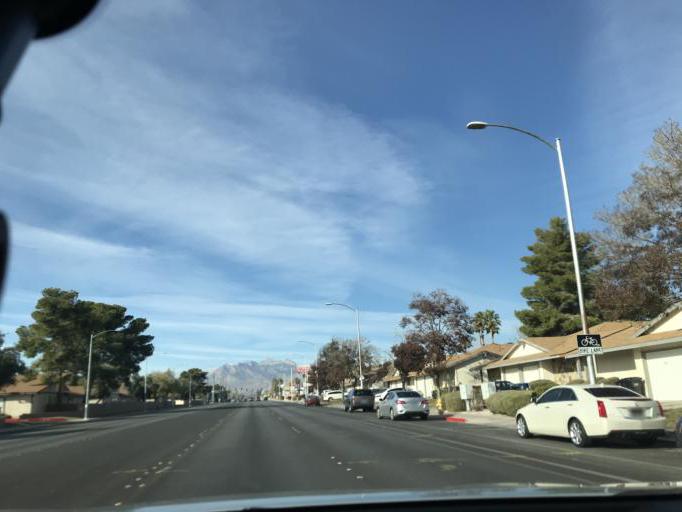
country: US
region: Nevada
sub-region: Clark County
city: Las Vegas
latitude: 36.2030
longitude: -115.2201
